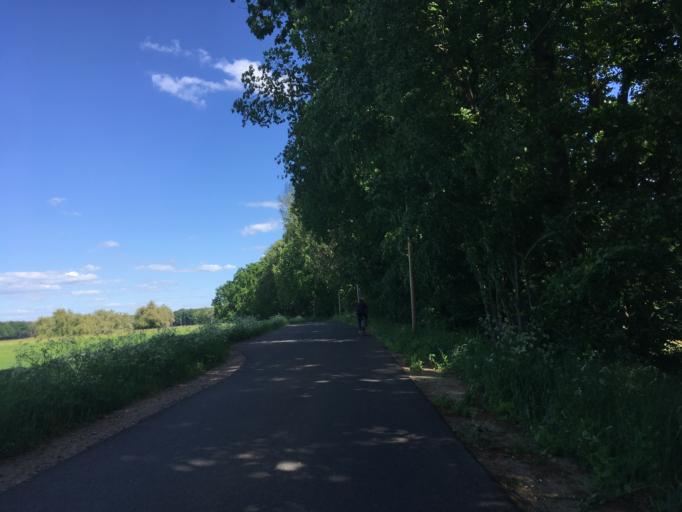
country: DE
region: Brandenburg
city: Joachimsthal
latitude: 52.9923
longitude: 13.7792
